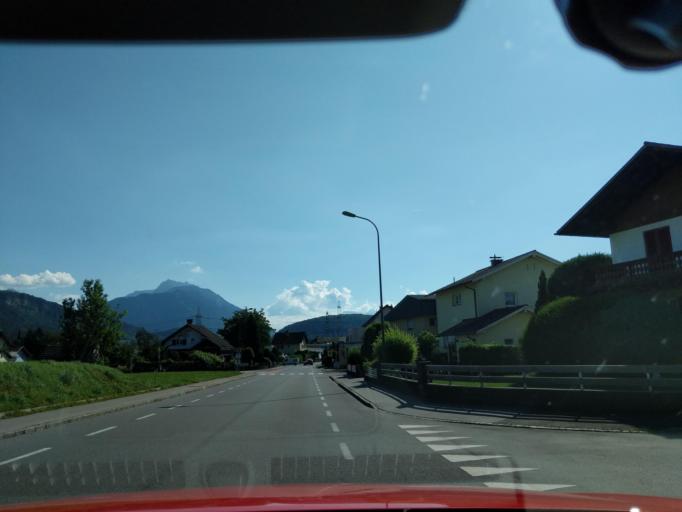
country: AT
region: Vorarlberg
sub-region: Politischer Bezirk Feldkirch
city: Rankweil
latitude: 47.2723
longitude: 9.6288
